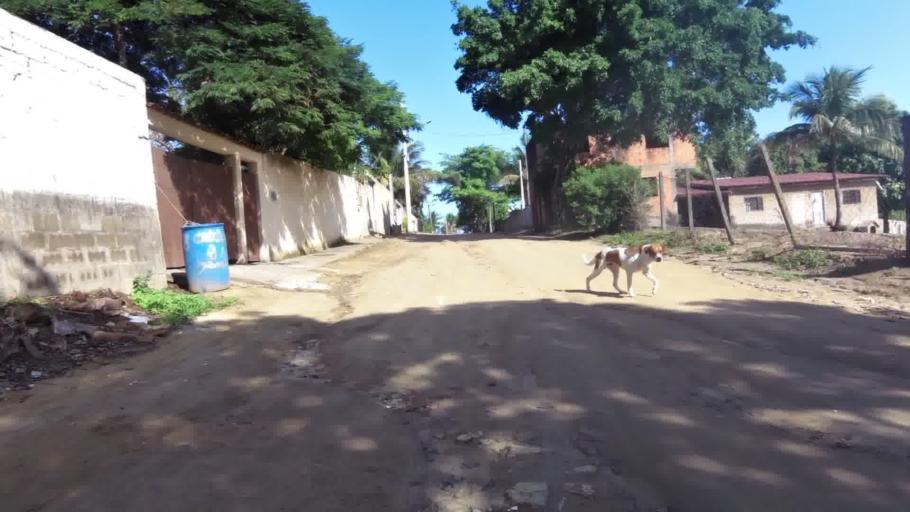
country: BR
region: Espirito Santo
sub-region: Piuma
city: Piuma
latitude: -20.8230
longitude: -40.6252
